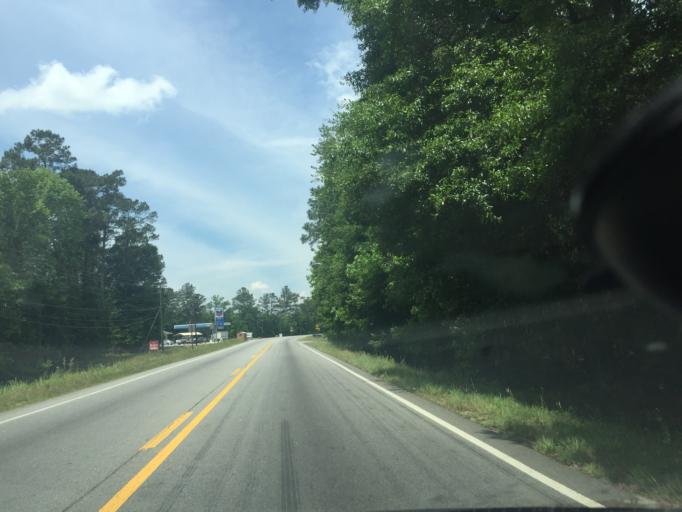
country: US
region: Georgia
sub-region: Chatham County
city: Bloomingdale
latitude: 32.1676
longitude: -81.3840
